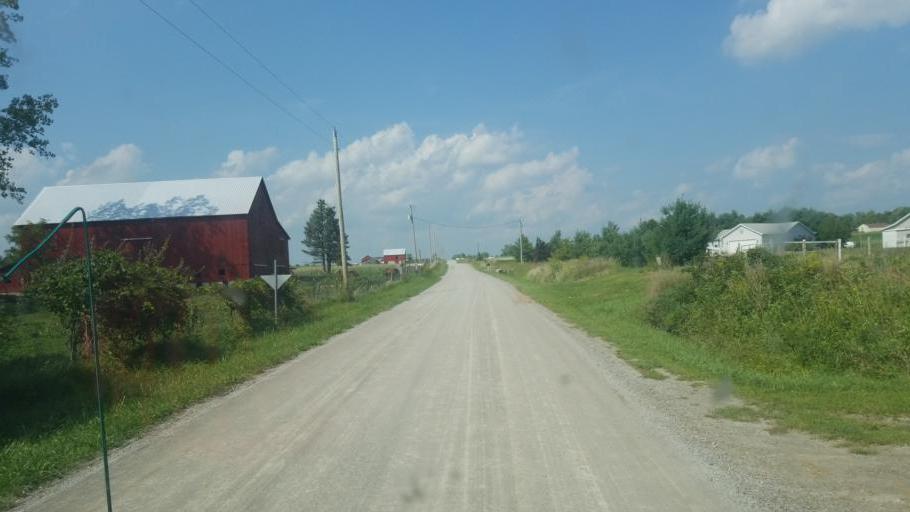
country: US
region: Ohio
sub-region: Wayne County
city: West Salem
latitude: 41.0455
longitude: -82.1449
